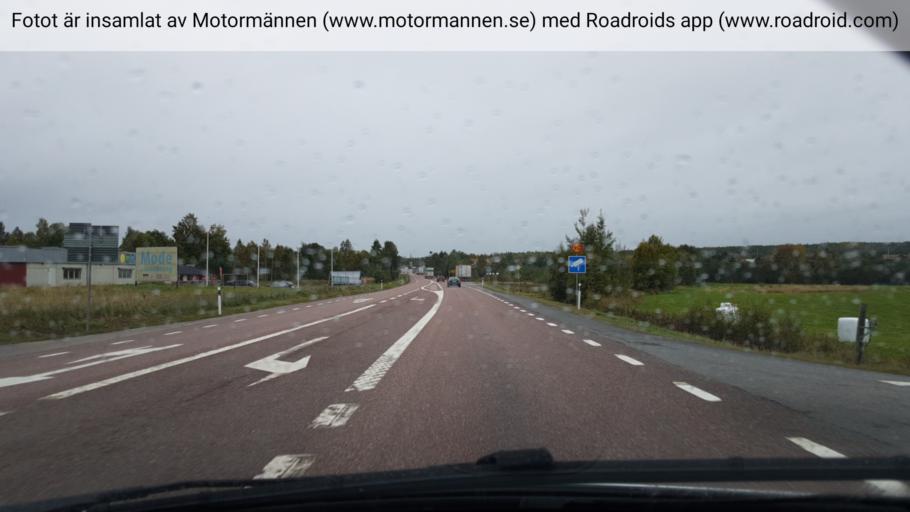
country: SE
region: Gaevleborg
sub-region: Nordanstigs Kommun
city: Bergsjoe
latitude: 61.9352
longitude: 17.2173
